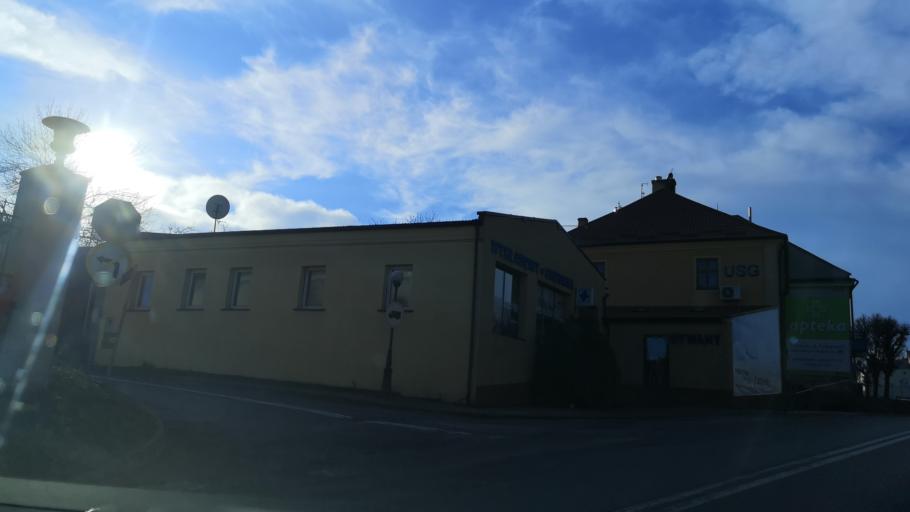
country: PL
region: Subcarpathian Voivodeship
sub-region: Powiat lezajski
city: Lezajsk
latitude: 50.2534
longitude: 22.4242
